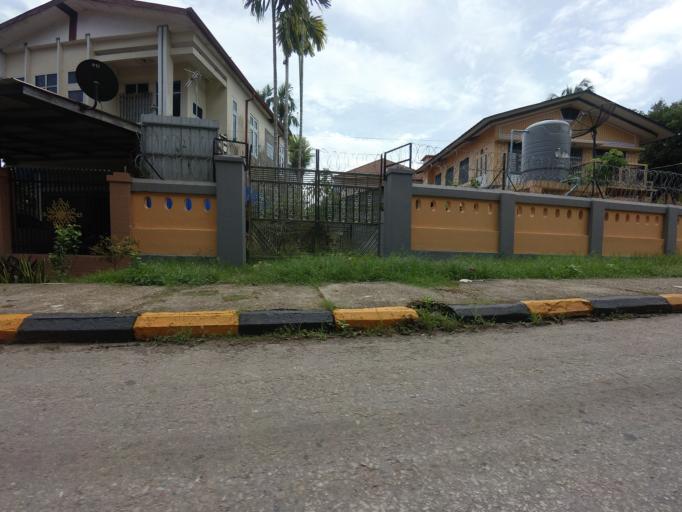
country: MM
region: Mon
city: Mawlamyine
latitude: 16.4771
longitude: 97.6244
